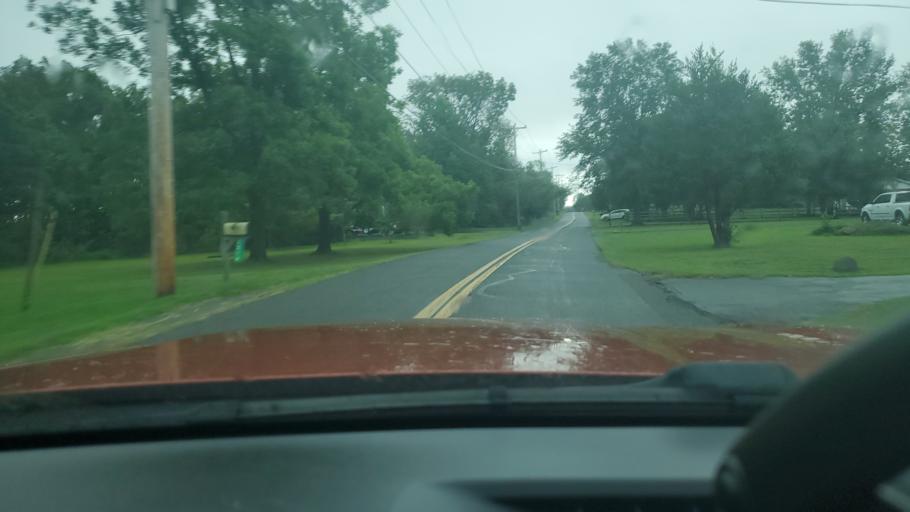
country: US
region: Pennsylvania
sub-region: Montgomery County
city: Spring Mount
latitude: 40.3031
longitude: -75.5042
